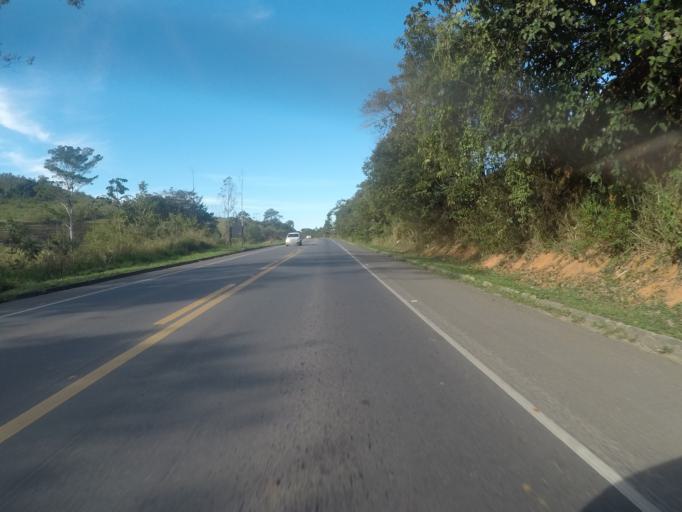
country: BR
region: Espirito Santo
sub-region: Ibiracu
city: Ibiracu
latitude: -19.8668
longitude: -40.3997
